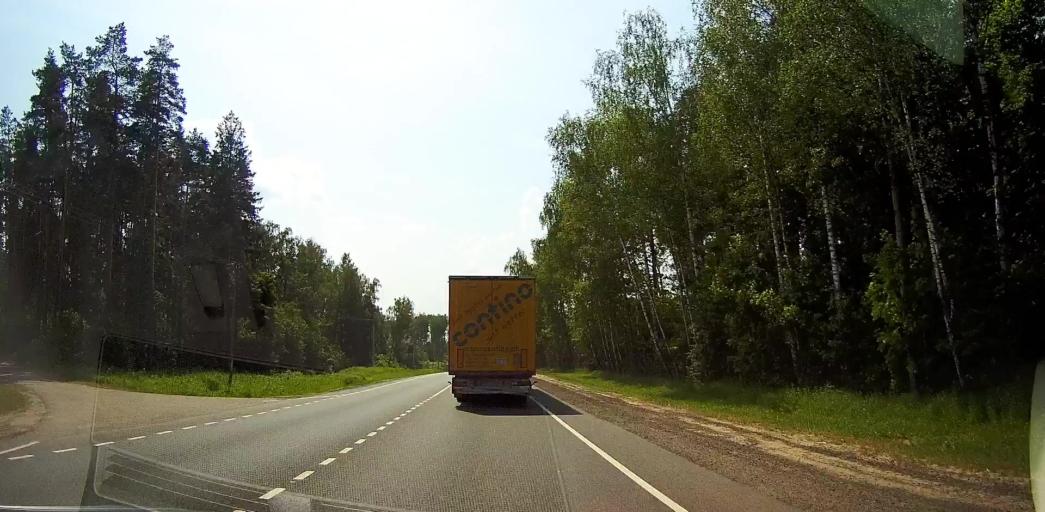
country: RU
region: Moskovskaya
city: Meshcherino
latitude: 55.2043
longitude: 38.3782
